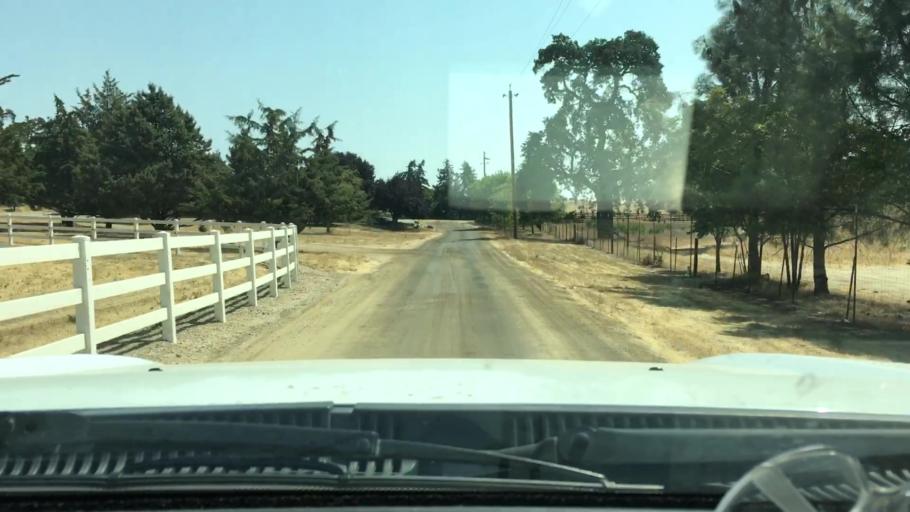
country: US
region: California
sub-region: San Luis Obispo County
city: Paso Robles
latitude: 35.5789
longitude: -120.6043
